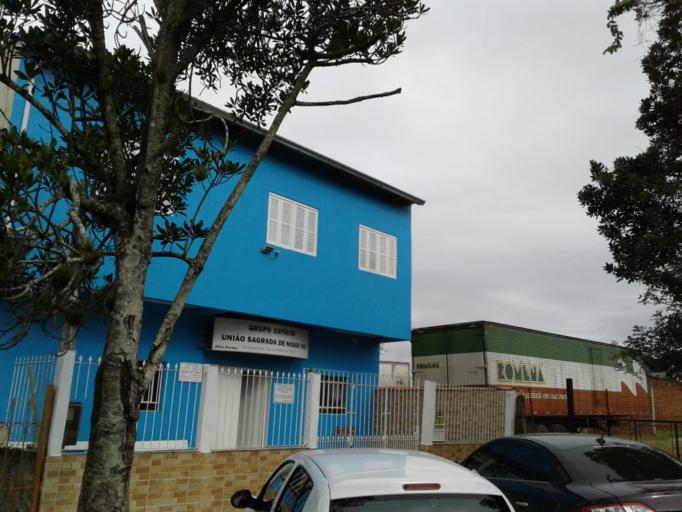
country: BR
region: Rio Grande do Sul
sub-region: Gravatai
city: Gravatai
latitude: -29.9366
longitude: -51.0057
